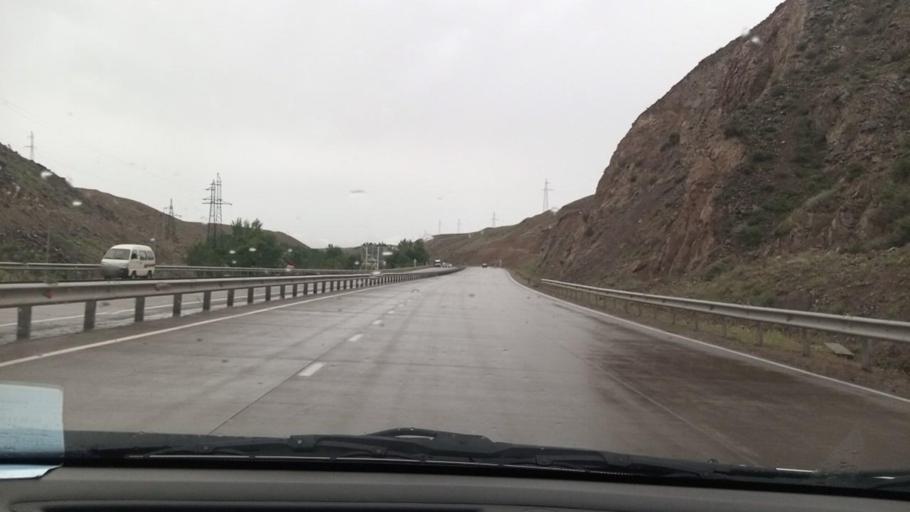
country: TJ
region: Viloyati Sughd
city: Shaydon
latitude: 40.9541
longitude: 70.6741
